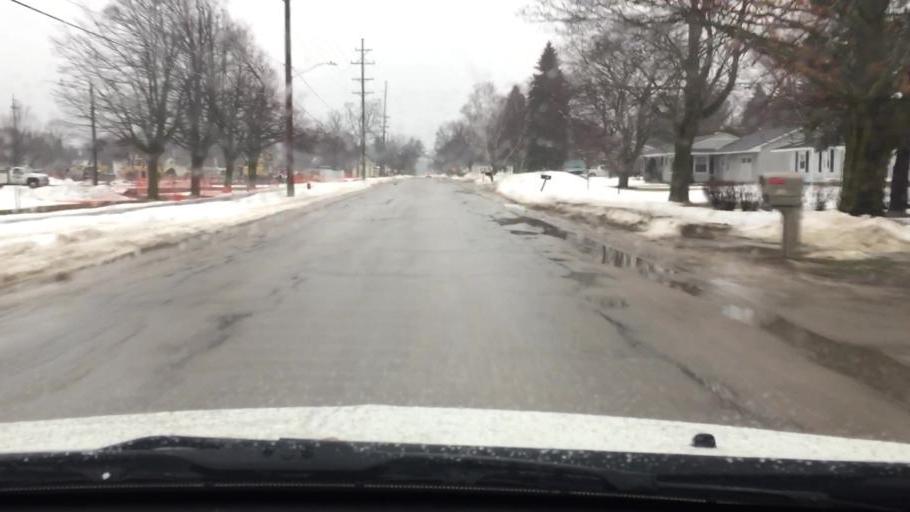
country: US
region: Michigan
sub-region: Charlevoix County
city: Charlevoix
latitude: 45.3097
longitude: -85.2554
